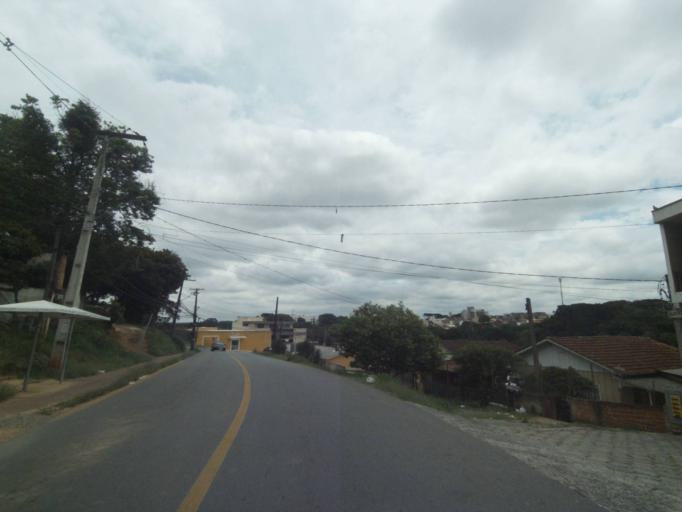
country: BR
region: Parana
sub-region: Curitiba
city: Curitiba
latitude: -25.3879
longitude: -49.2898
